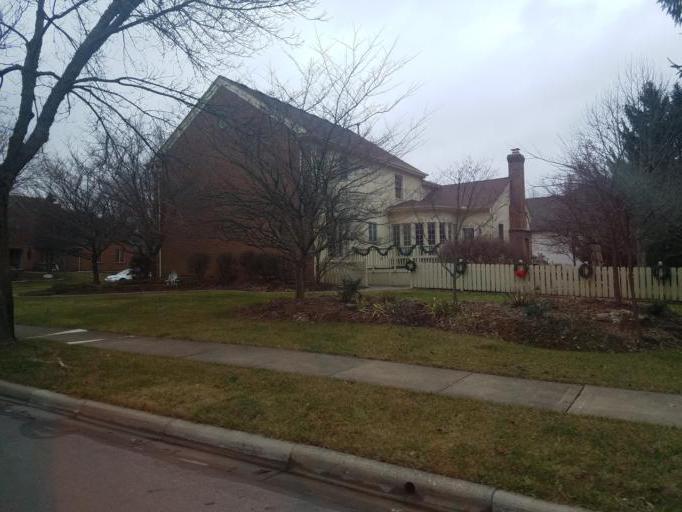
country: US
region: Ohio
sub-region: Franklin County
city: Westerville
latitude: 40.1356
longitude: -82.9559
